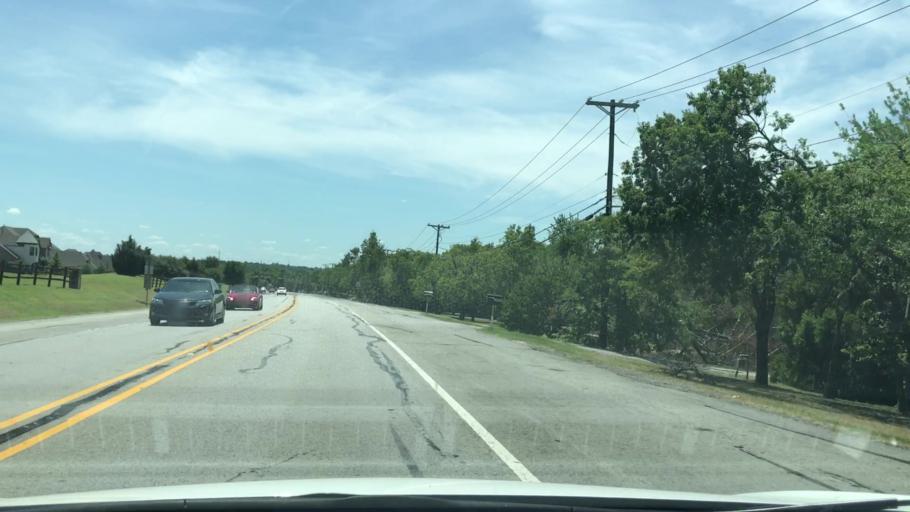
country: US
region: Texas
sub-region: Rockwall County
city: Rockwall
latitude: 32.9612
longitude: -96.4648
